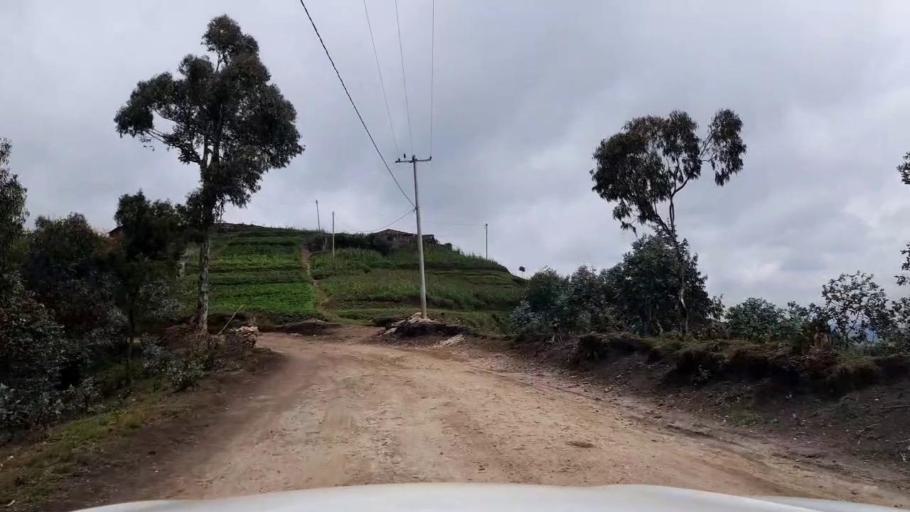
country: RW
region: Western Province
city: Kibuye
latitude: -1.9387
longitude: 29.4643
